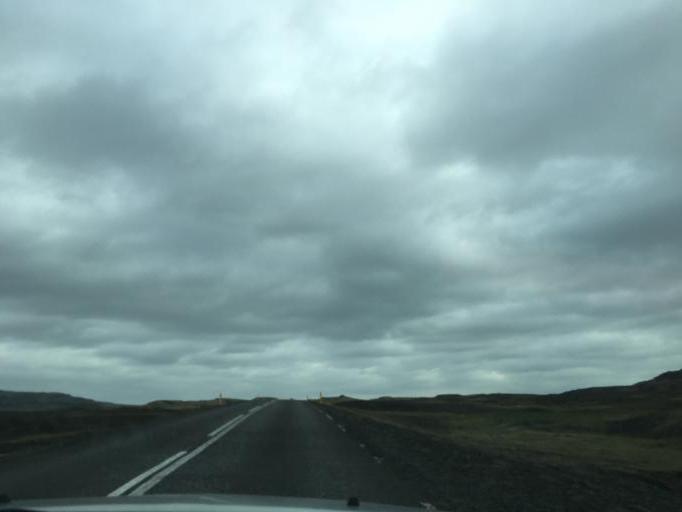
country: IS
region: South
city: Vestmannaeyjar
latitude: 64.2503
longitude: -20.2045
